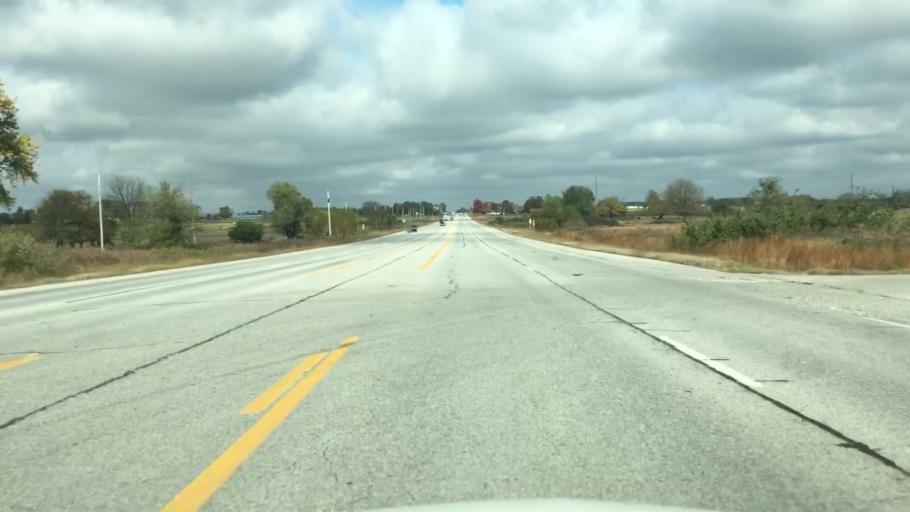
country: US
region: Arkansas
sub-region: Benton County
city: Siloam Springs
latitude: 36.2096
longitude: -94.4957
